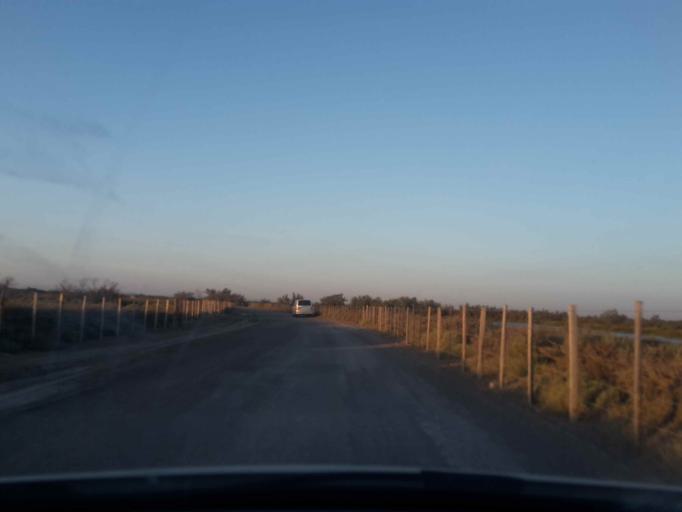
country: FR
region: Provence-Alpes-Cote d'Azur
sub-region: Departement des Bouches-du-Rhone
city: Port-Saint-Louis-du-Rhone
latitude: 43.4060
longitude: 4.6753
